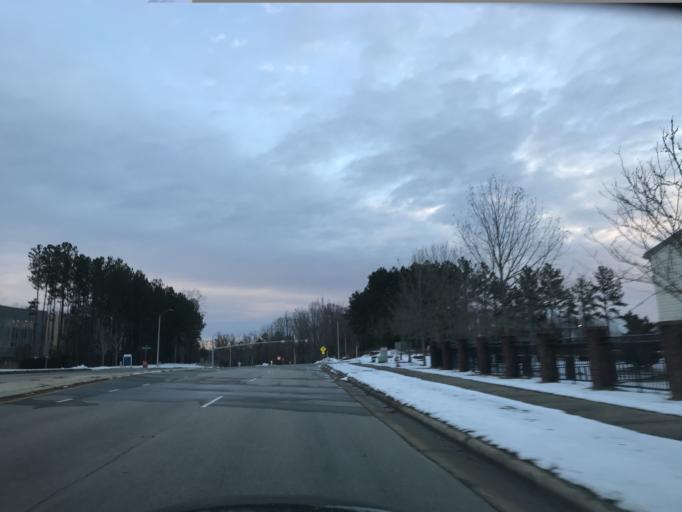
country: US
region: North Carolina
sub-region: Wake County
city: Knightdale
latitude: 35.8649
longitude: -78.5379
